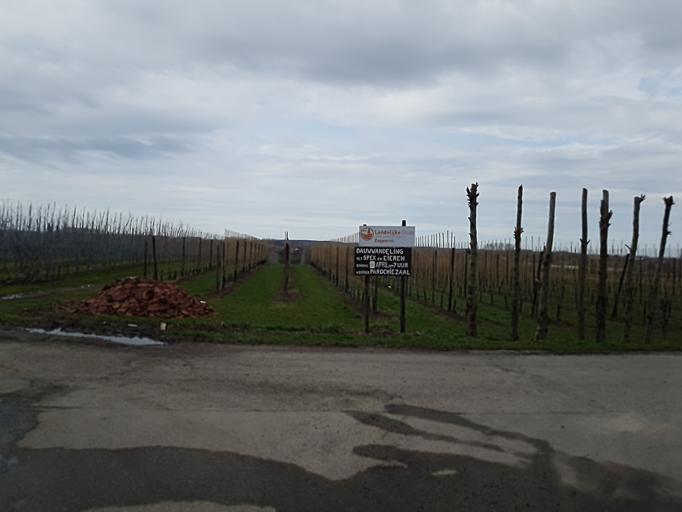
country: BE
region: Flanders
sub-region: Provincie Limburg
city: Alken
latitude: 50.8164
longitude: 5.2614
